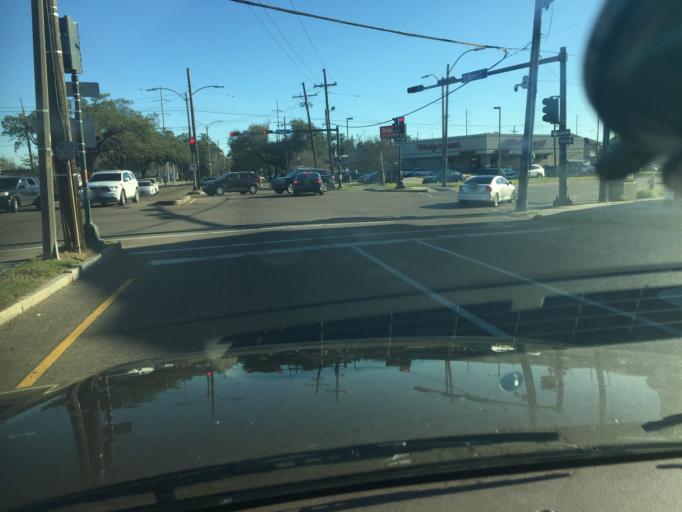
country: US
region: Louisiana
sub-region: Orleans Parish
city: New Orleans
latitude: 29.9836
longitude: -90.0719
